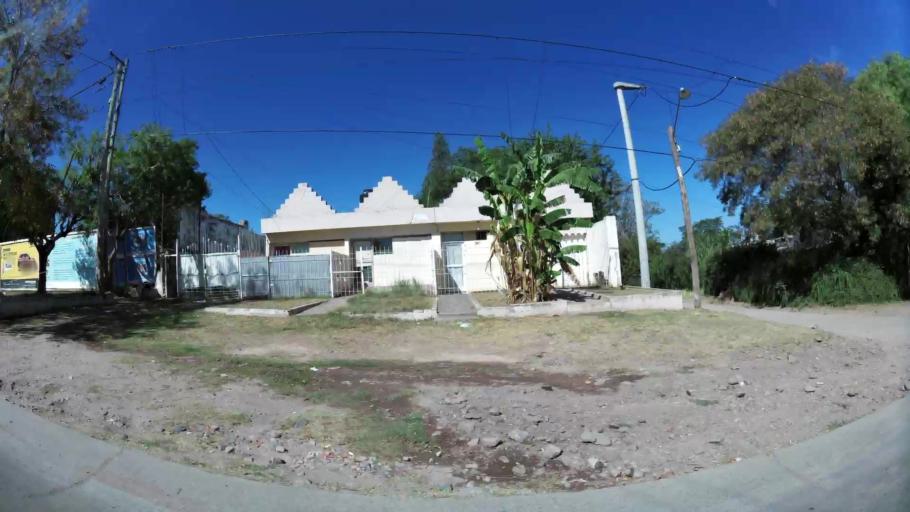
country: AR
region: Cordoba
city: Villa Allende
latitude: -31.3143
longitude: -64.2882
